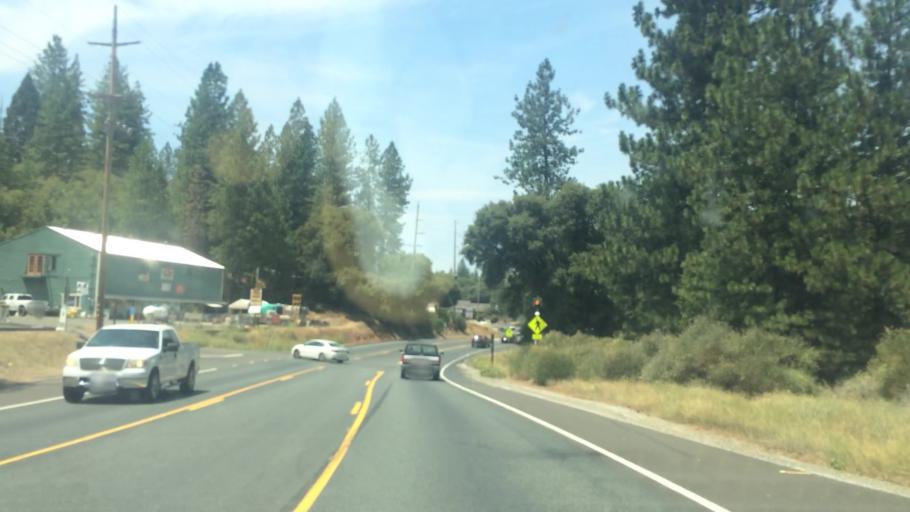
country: US
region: California
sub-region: Amador County
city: Pine Grove
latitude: 38.4104
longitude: -120.6517
